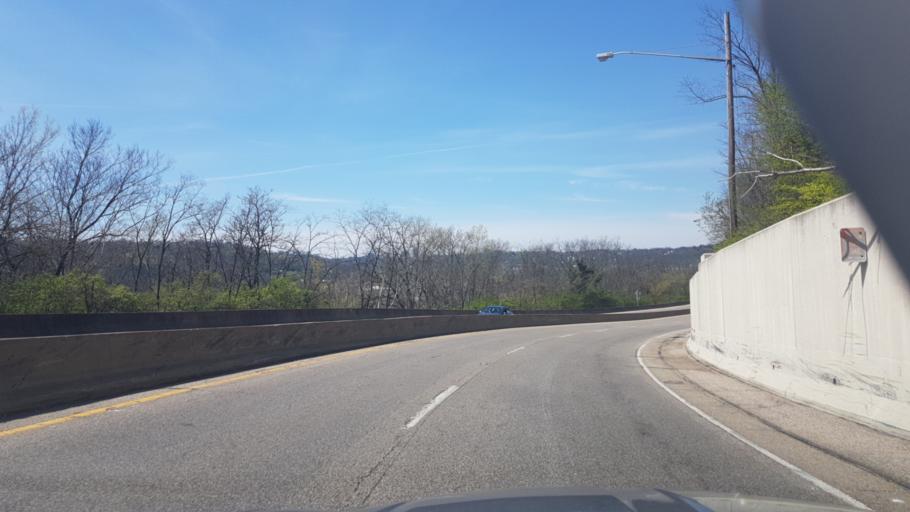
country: US
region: Kentucky
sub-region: Campbell County
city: Fort Thomas
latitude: 39.1081
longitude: -84.4294
